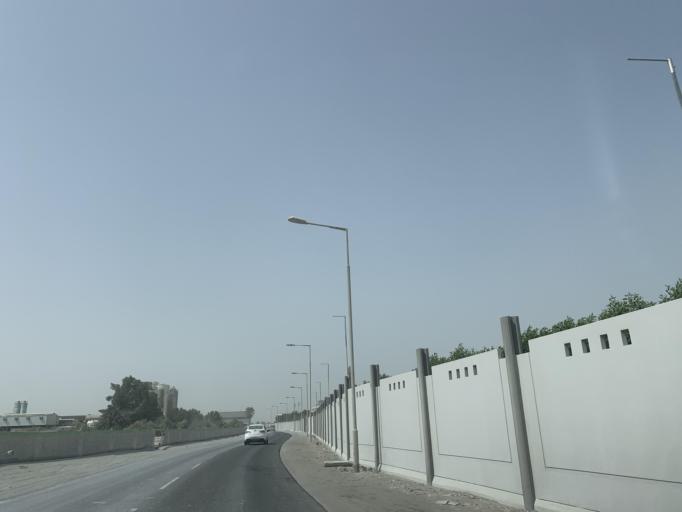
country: BH
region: Northern
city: Madinat `Isa
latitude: 26.1837
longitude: 50.5174
